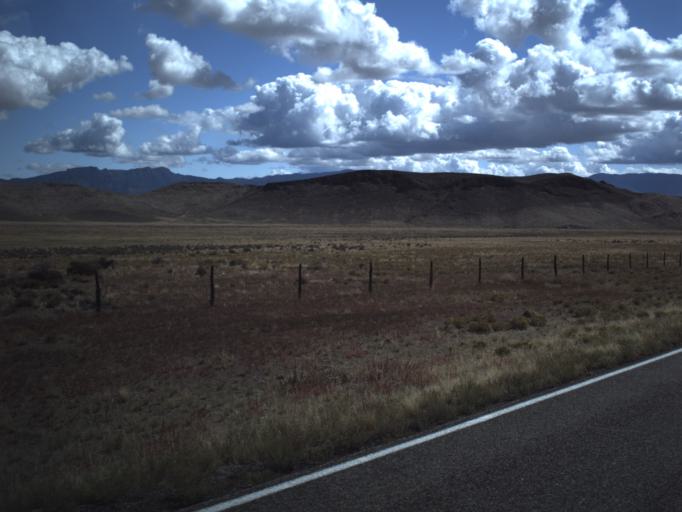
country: US
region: Utah
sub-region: Beaver County
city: Milford
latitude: 38.6019
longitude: -113.8326
